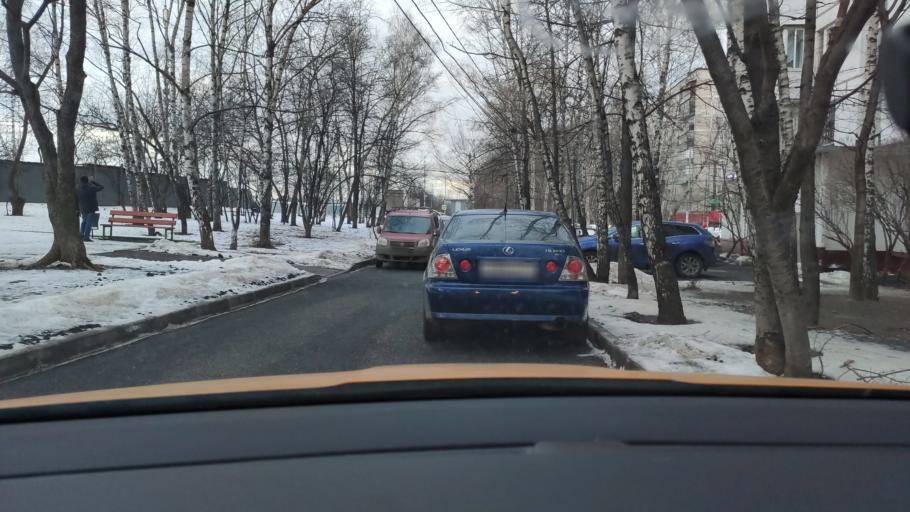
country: RU
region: Moscow
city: Tsaritsyno
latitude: 55.6169
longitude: 37.6454
